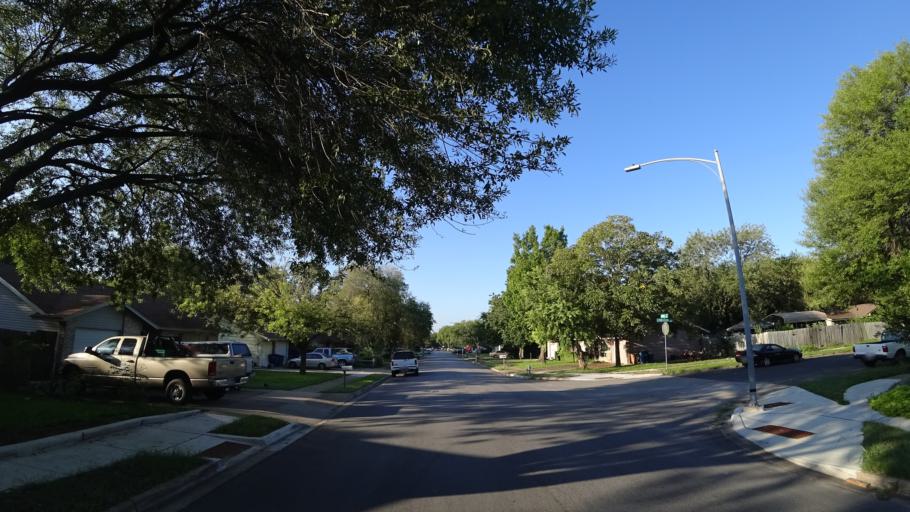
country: US
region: Texas
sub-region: Travis County
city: Wells Branch
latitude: 30.3640
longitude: -97.6883
